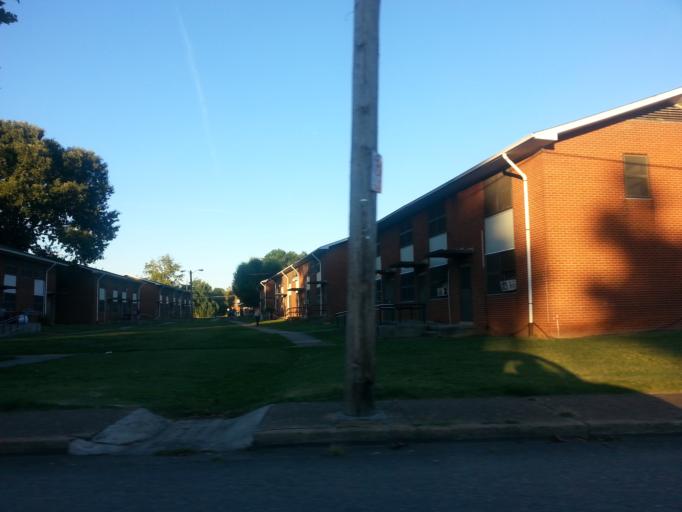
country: US
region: Tennessee
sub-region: Knox County
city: Knoxville
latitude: 35.9721
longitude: -83.9092
